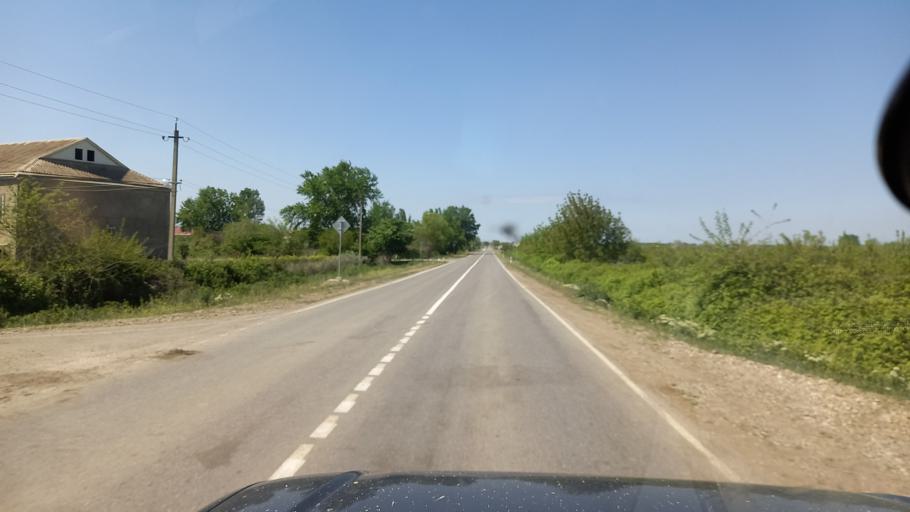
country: RU
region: Dagestan
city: Novaya Maka
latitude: 41.8152
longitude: 48.4033
